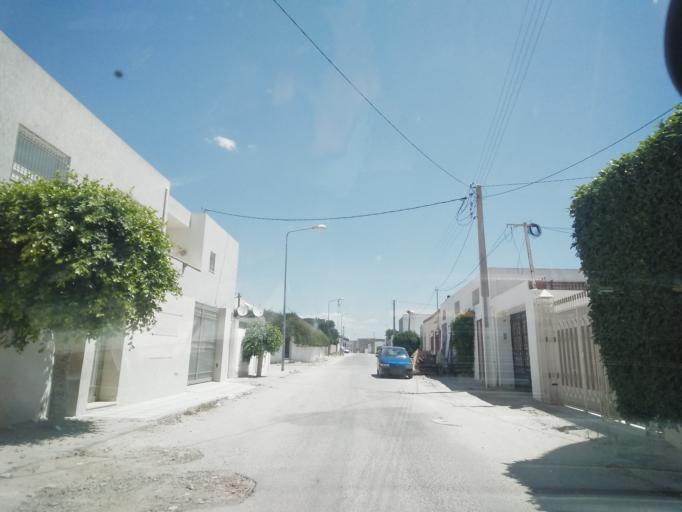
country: TN
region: Safaqis
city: Al Qarmadah
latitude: 34.8220
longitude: 10.7669
